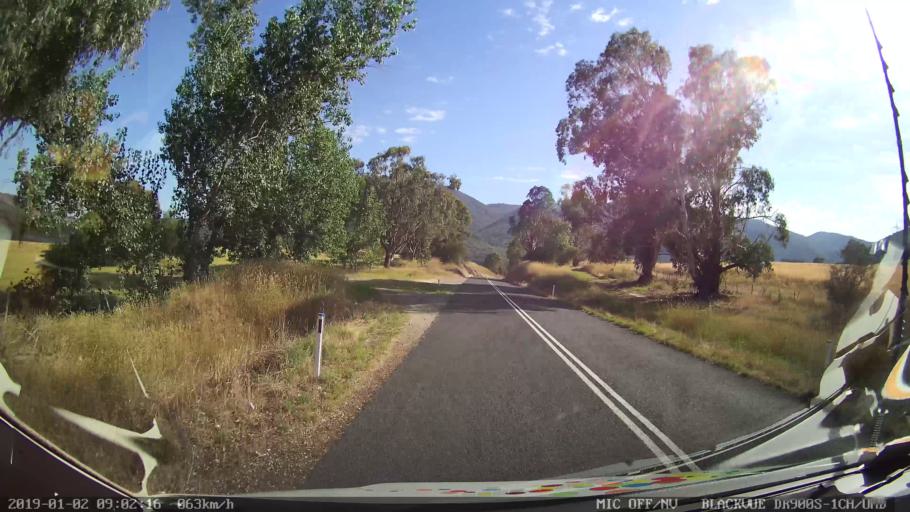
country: AU
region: New South Wales
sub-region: Tumut Shire
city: Tumut
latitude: -35.5743
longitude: 148.3115
